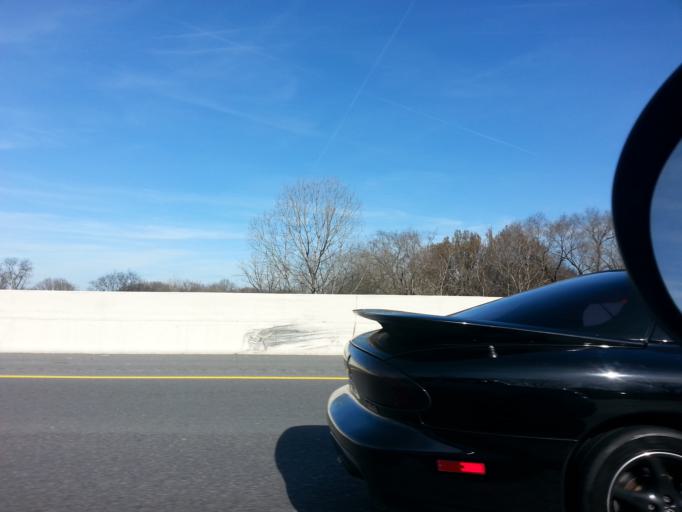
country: US
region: Tennessee
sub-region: Davidson County
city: Oak Hill
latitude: 36.1174
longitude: -86.7259
